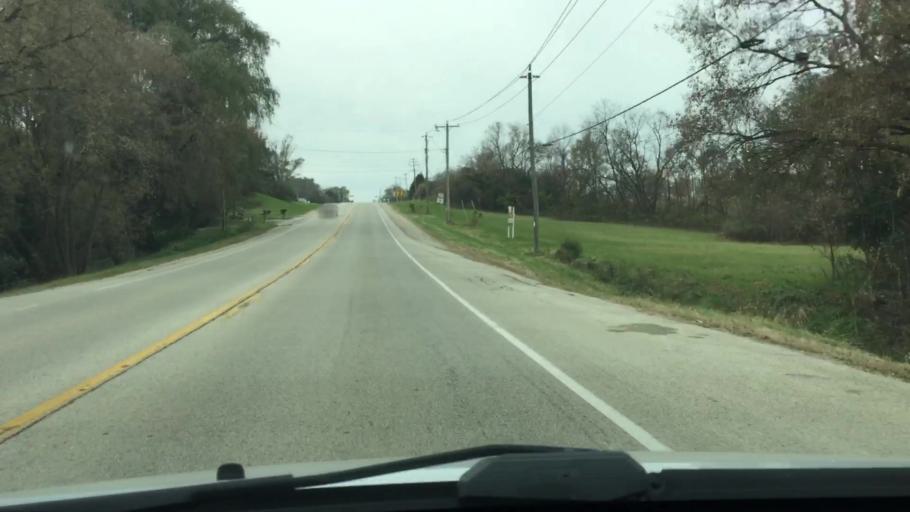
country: US
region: Wisconsin
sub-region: Waukesha County
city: Muskego
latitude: 42.9487
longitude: -88.1518
